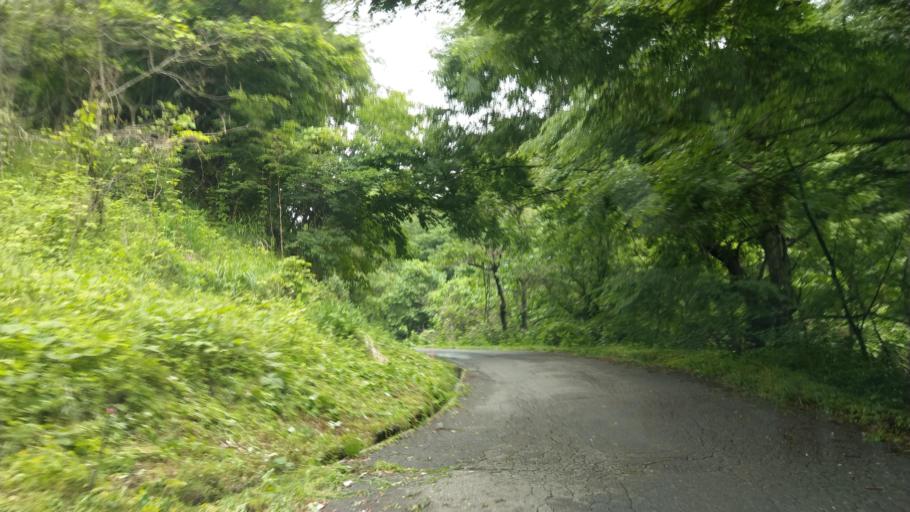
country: JP
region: Nagano
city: Komoro
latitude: 36.3162
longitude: 138.4063
